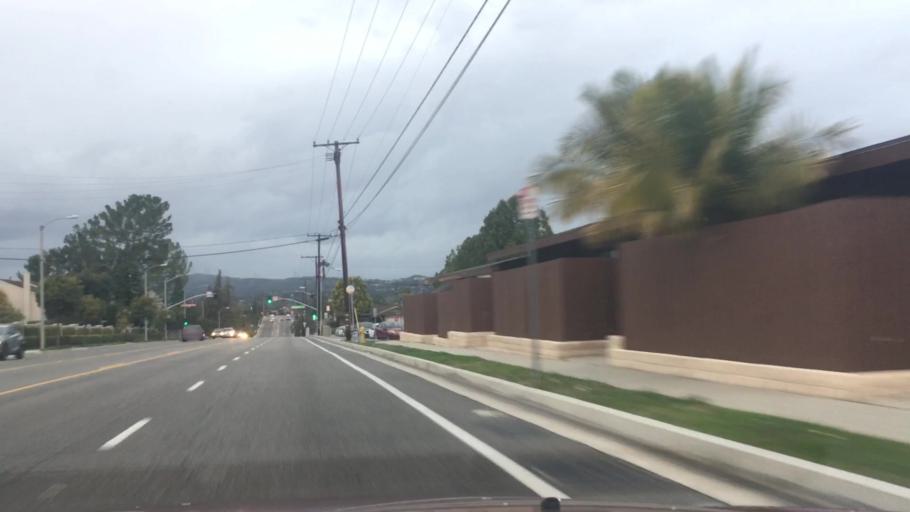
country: US
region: California
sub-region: Los Angeles County
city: East La Mirada
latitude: 33.9187
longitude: -117.9943
